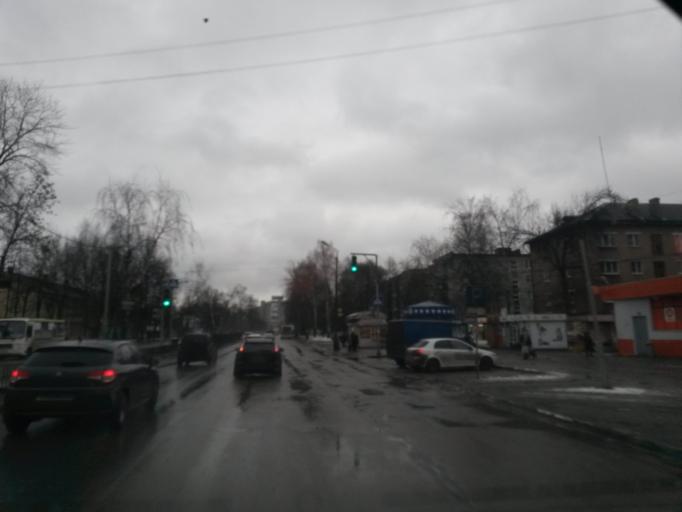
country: RU
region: Jaroslavl
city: Yaroslavl
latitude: 57.6524
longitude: 39.9351
